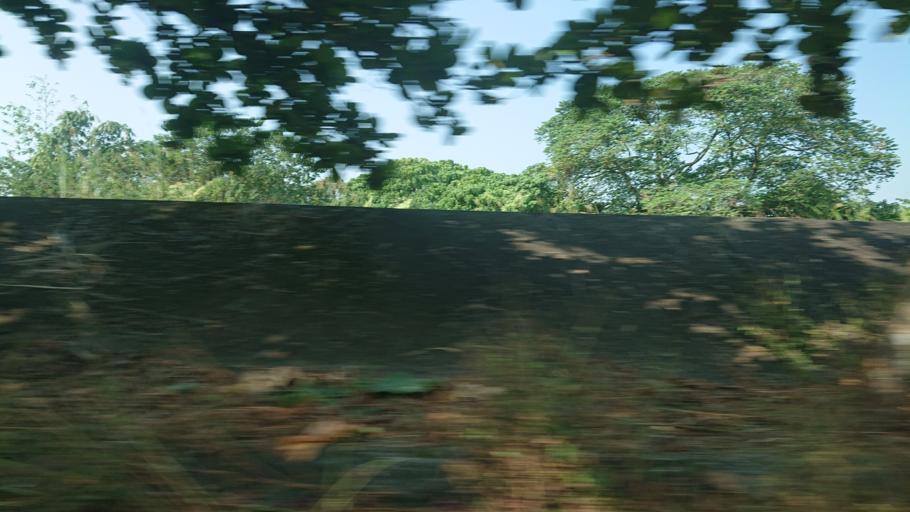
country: TW
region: Taiwan
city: Lugu
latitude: 23.7400
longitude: 120.6583
